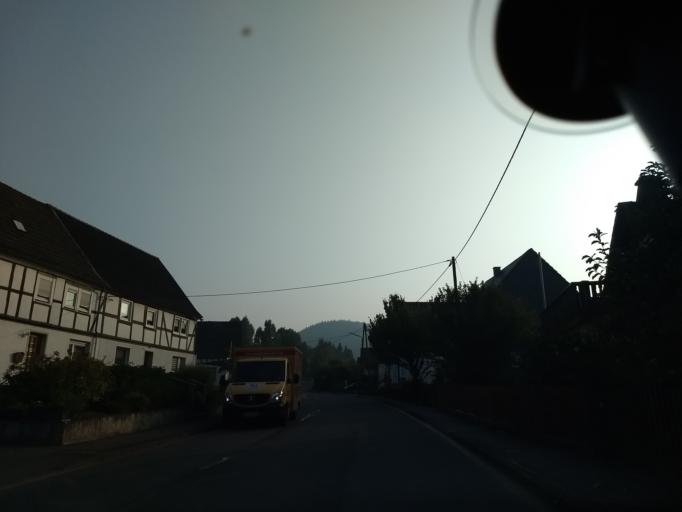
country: DE
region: North Rhine-Westphalia
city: Eslohe
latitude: 51.2136
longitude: 8.0817
